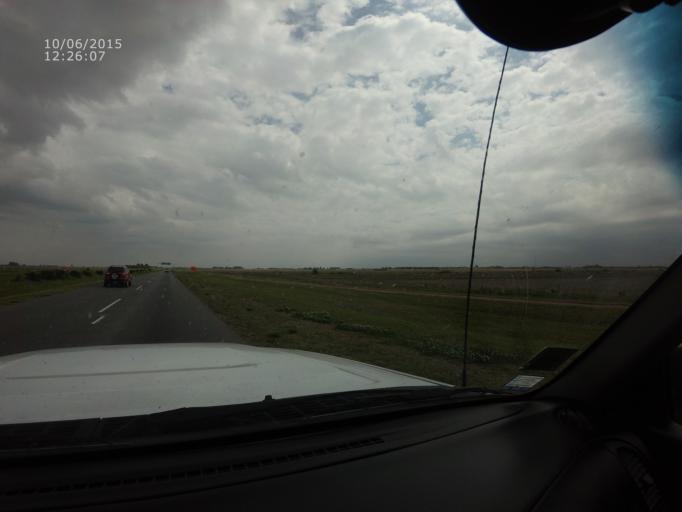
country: AR
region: Santa Fe
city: Roldan
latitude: -32.9044
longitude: -61.0120
